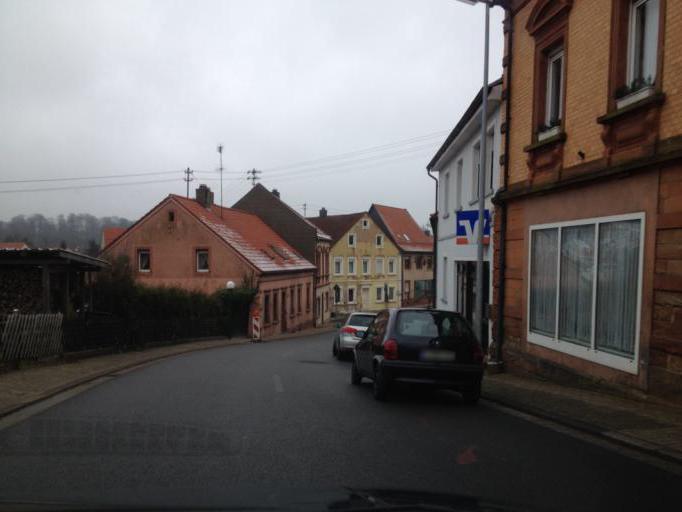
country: DE
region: Rheinland-Pfalz
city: Dunzweiler
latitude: 49.3889
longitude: 7.2711
